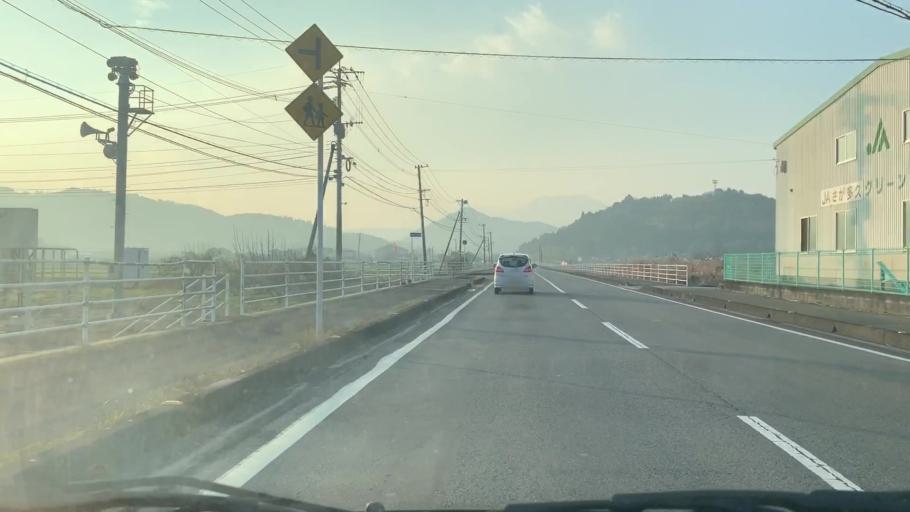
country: JP
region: Saga Prefecture
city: Takeocho-takeo
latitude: 33.2719
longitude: 130.1330
